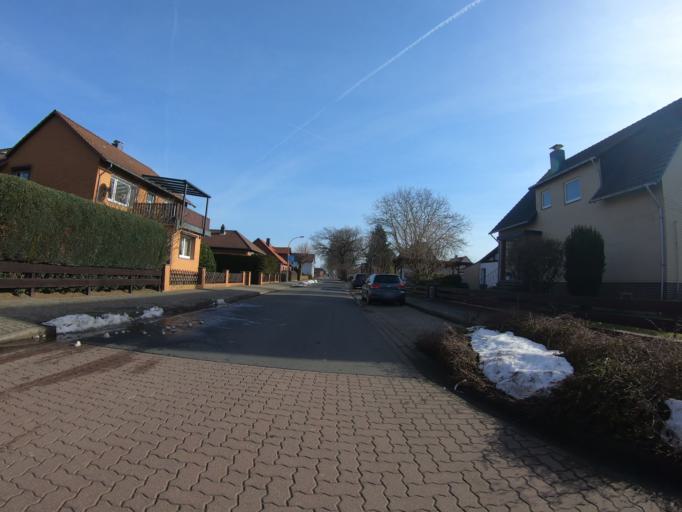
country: DE
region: Lower Saxony
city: Vordorf
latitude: 52.3653
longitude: 10.5192
